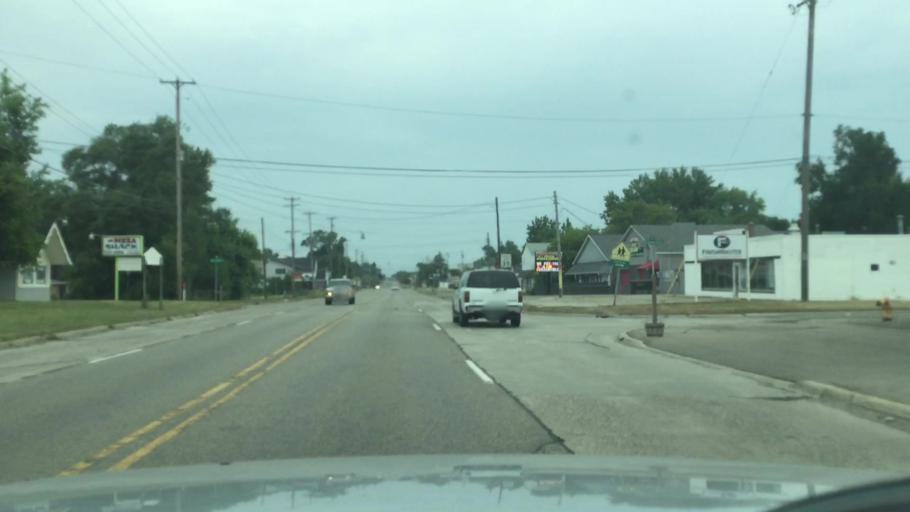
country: US
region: Michigan
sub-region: Genesee County
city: Flint
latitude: 42.9684
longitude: -83.6928
